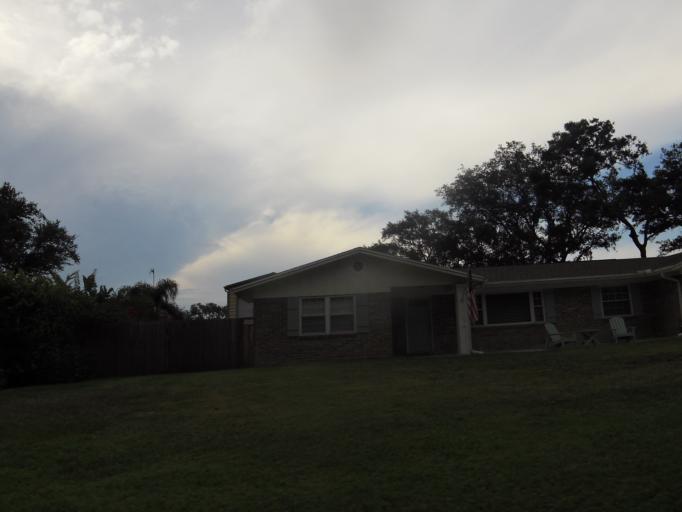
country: US
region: Florida
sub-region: Duval County
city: Jacksonville Beach
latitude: 30.2785
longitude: -81.4062
